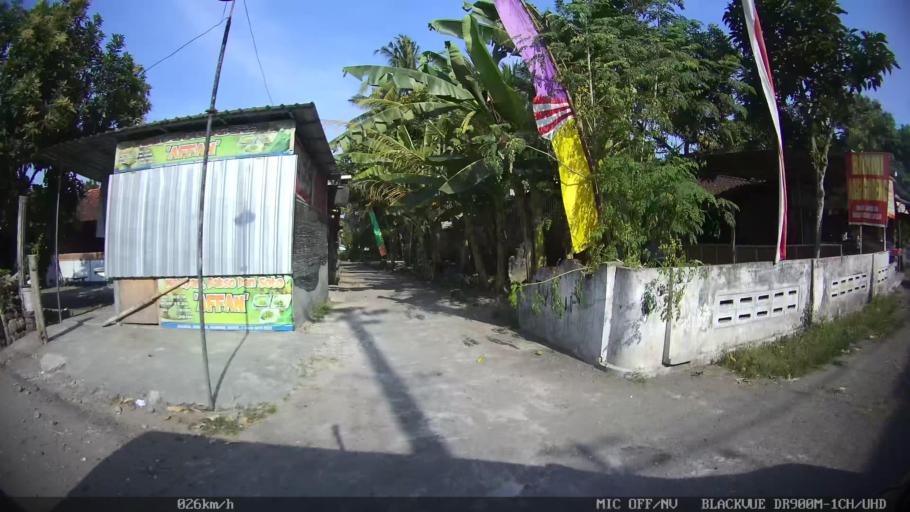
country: ID
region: Daerah Istimewa Yogyakarta
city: Pandak
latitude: -7.8931
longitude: 110.2996
